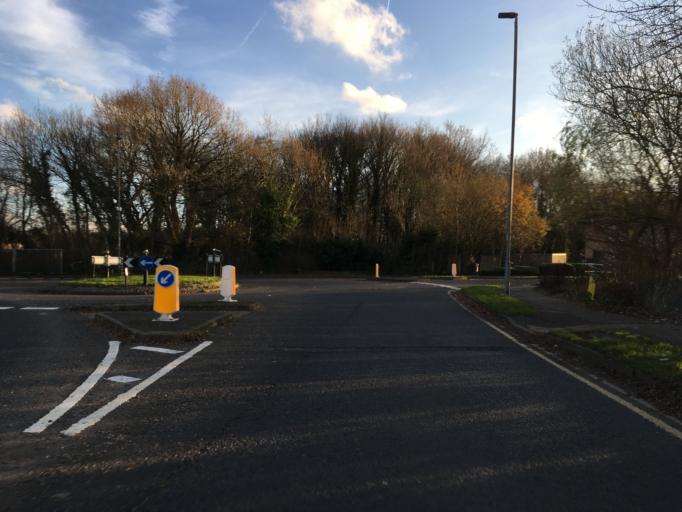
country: GB
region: England
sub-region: Cheshire East
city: Wilmslow
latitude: 53.3495
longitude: -2.2099
